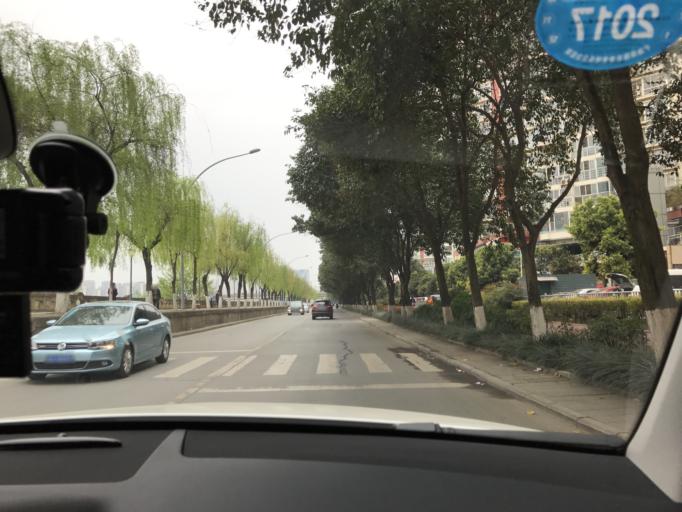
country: CN
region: Sichuan
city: Mianyang
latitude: 31.4535
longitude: 104.7096
